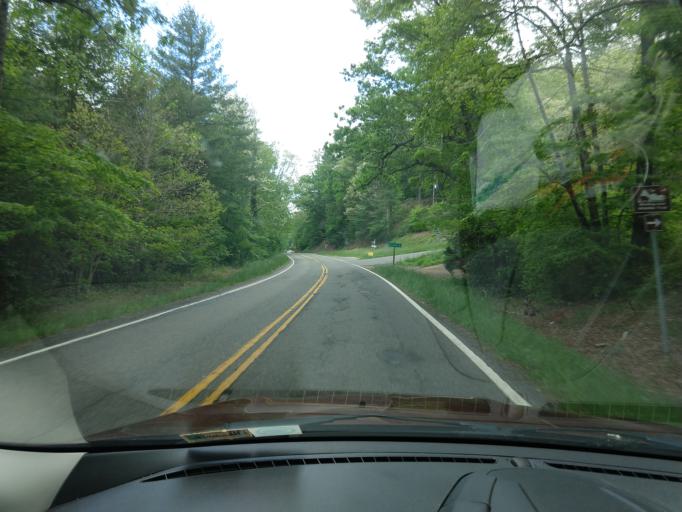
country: US
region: Virginia
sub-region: City of Galax
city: Galax
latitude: 36.7869
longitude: -80.9833
